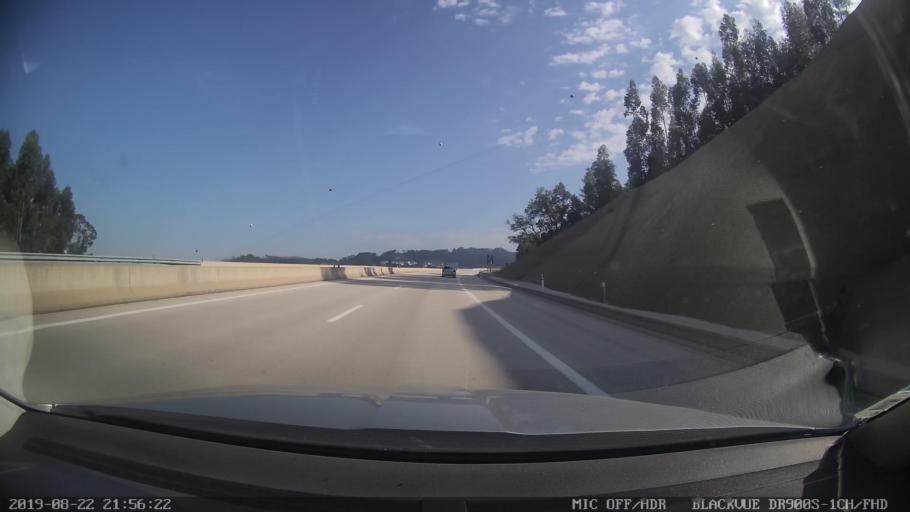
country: PT
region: Coimbra
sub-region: Coimbra
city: Coimbra
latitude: 40.1689
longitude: -8.3785
